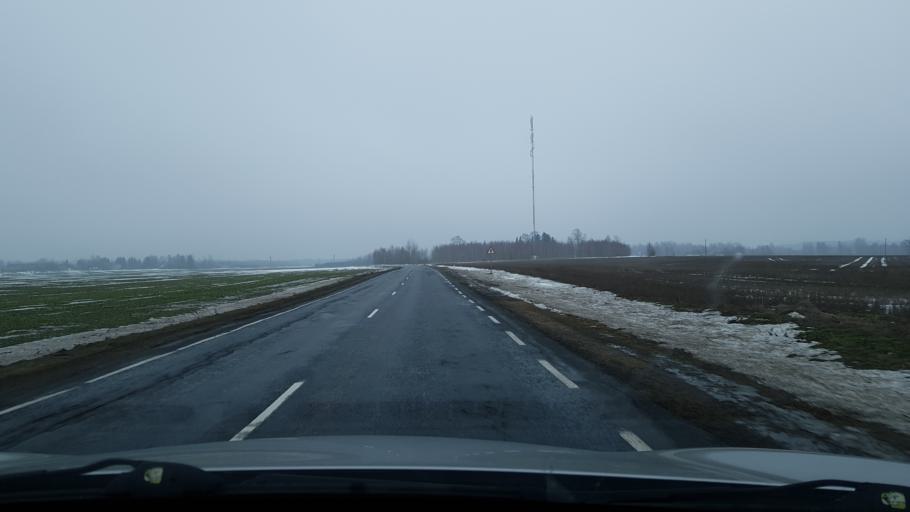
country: EE
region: Valgamaa
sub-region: Torva linn
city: Torva
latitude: 58.1571
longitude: 25.9634
